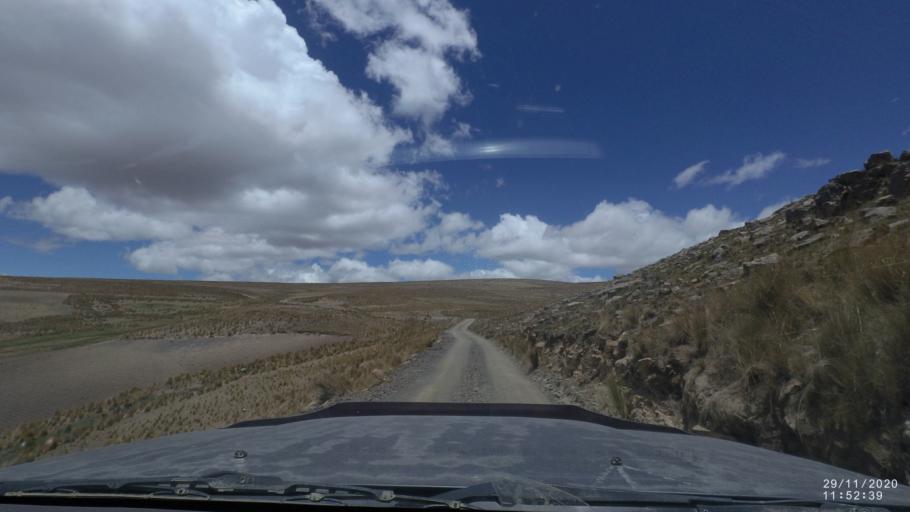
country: BO
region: Cochabamba
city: Cochabamba
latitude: -17.1683
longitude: -66.2663
